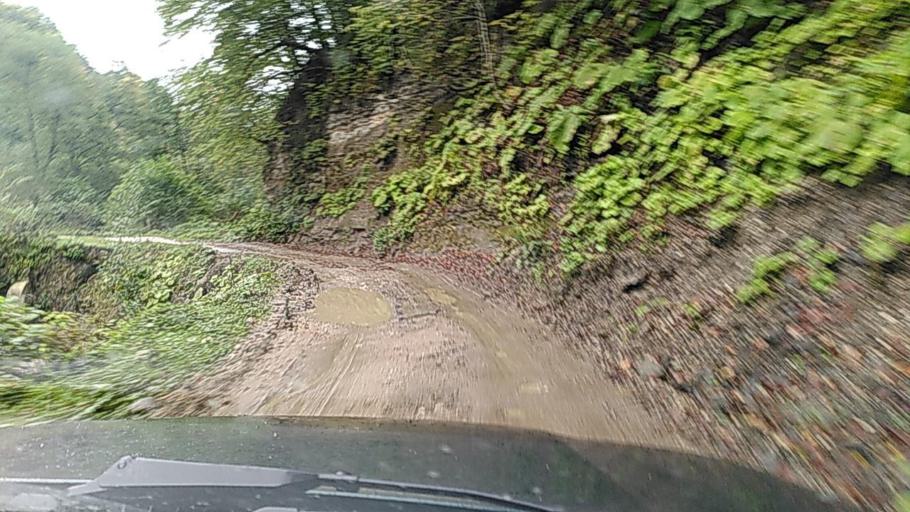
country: RU
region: Kabardino-Balkariya
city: Belaya Rechka
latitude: 43.4036
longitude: 43.4635
